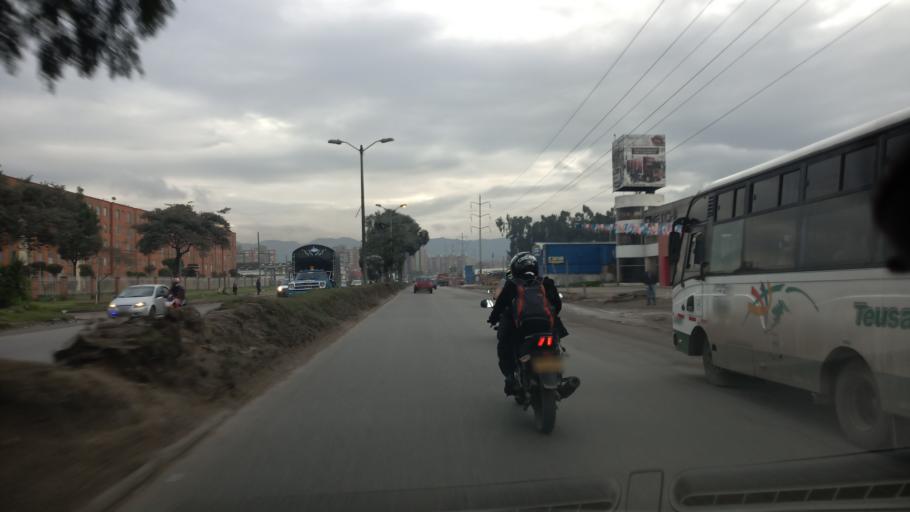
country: CO
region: Bogota D.C.
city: Bogota
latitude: 4.6652
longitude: -74.1444
